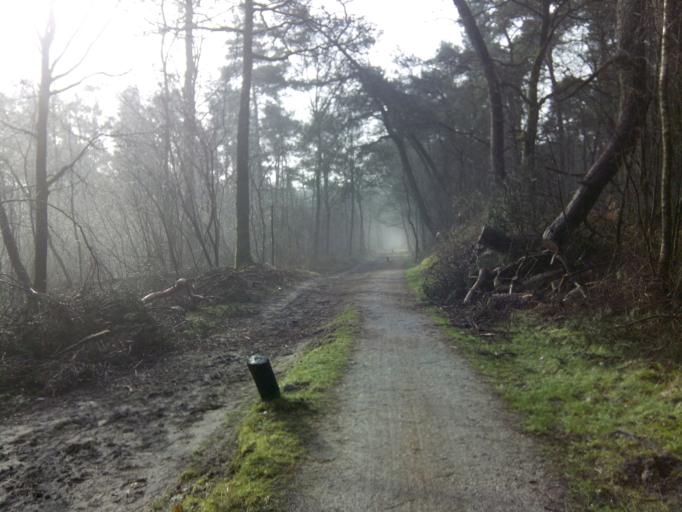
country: NL
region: Utrecht
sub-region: Gemeente Utrechtse Heuvelrug
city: Leersum
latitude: 52.0258
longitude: 5.4263
